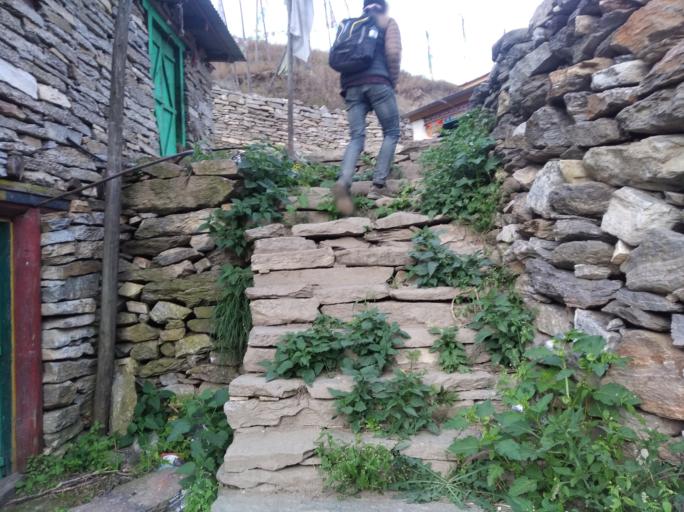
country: NP
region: Western Region
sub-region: Dhawalagiri Zone
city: Jomsom
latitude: 28.8797
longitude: 82.9878
